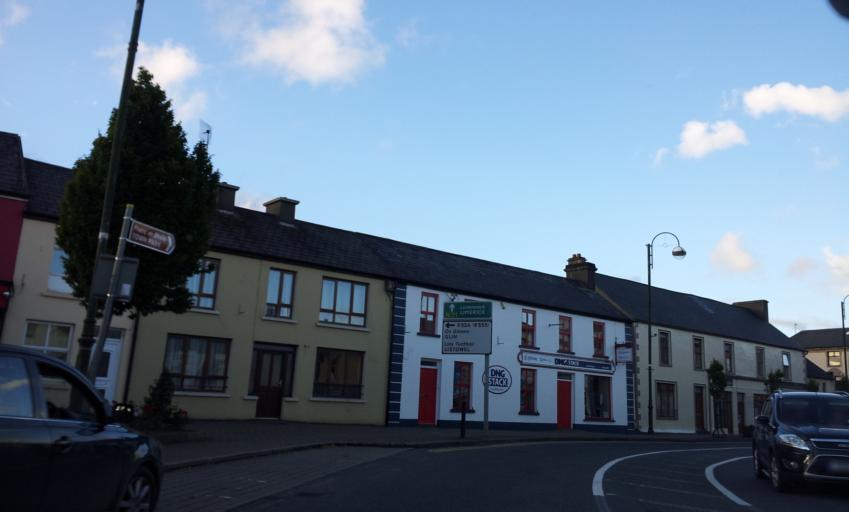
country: IE
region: Munster
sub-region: County Limerick
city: Abbeyfeale
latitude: 52.3846
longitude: -9.3016
